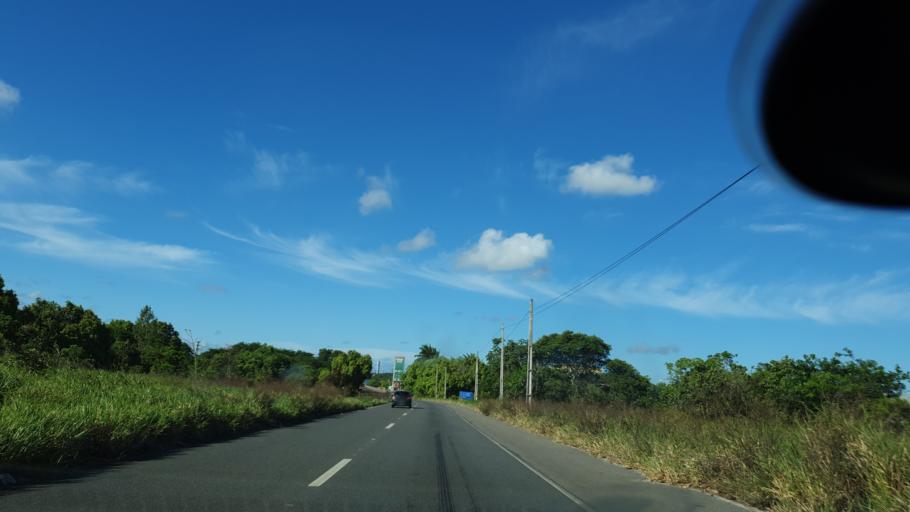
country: BR
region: Bahia
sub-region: Camacari
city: Camacari
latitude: -12.6763
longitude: -38.3010
